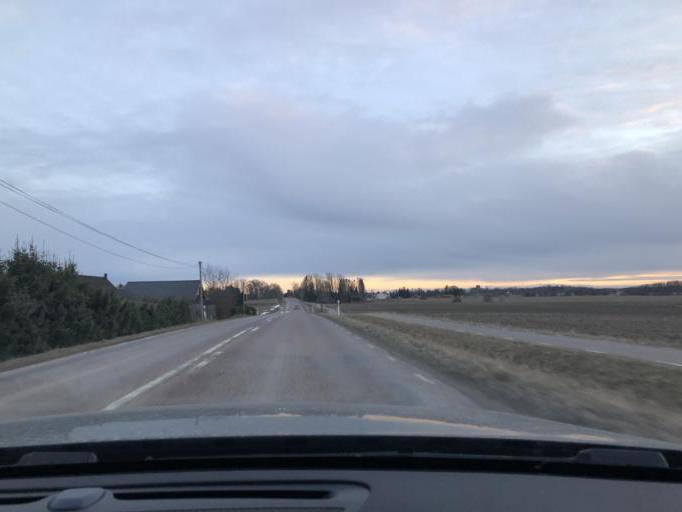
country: SE
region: Uppsala
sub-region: Uppsala Kommun
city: Gamla Uppsala
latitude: 59.9192
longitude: 17.6422
